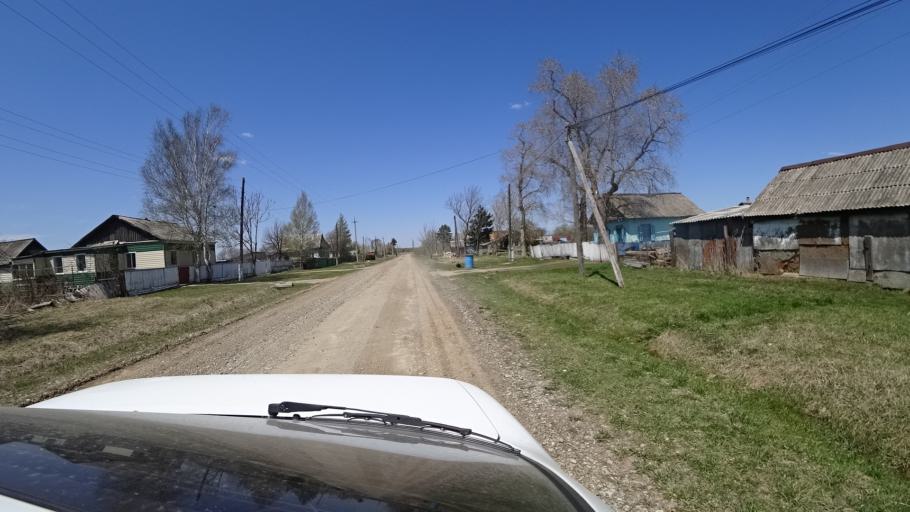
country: RU
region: Primorskiy
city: Lazo
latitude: 45.7990
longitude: 133.7638
